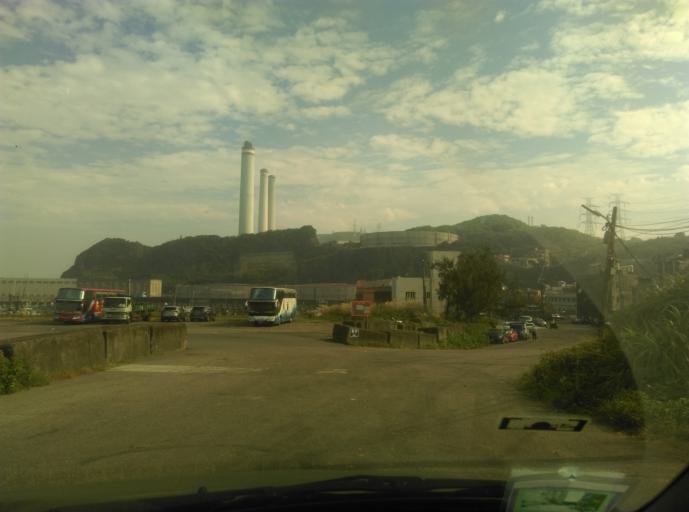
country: TW
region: Taiwan
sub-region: Keelung
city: Keelung
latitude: 25.1603
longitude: 121.7322
